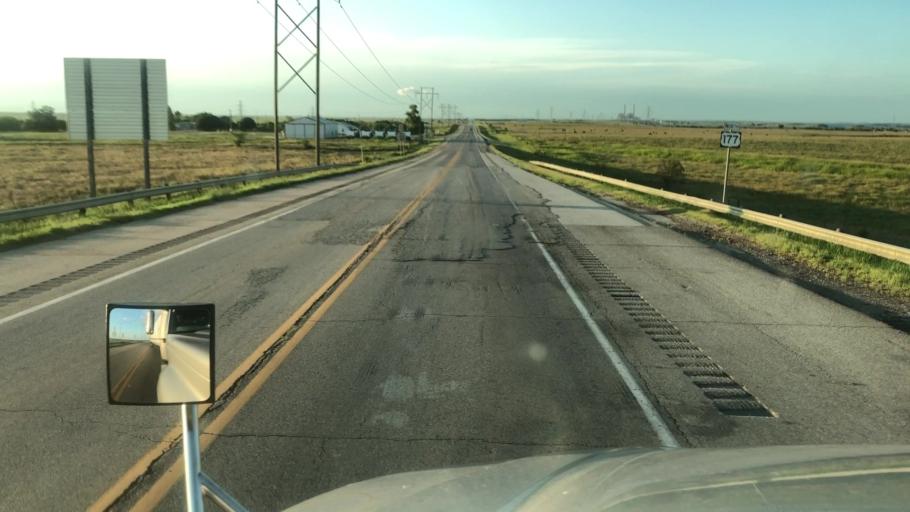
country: US
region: Oklahoma
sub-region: Noble County
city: Perry
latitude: 36.3857
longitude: -97.0677
